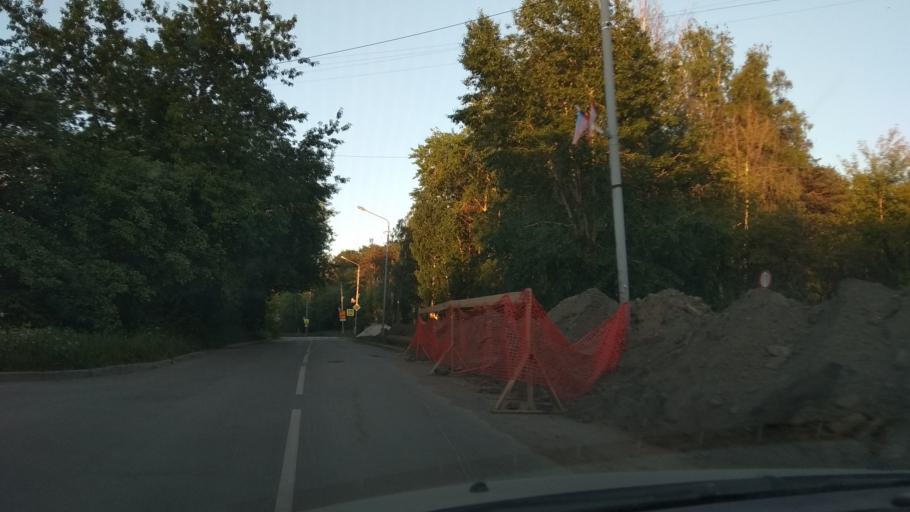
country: RU
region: Sverdlovsk
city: Sredneuralsk
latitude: 56.9888
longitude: 60.4656
